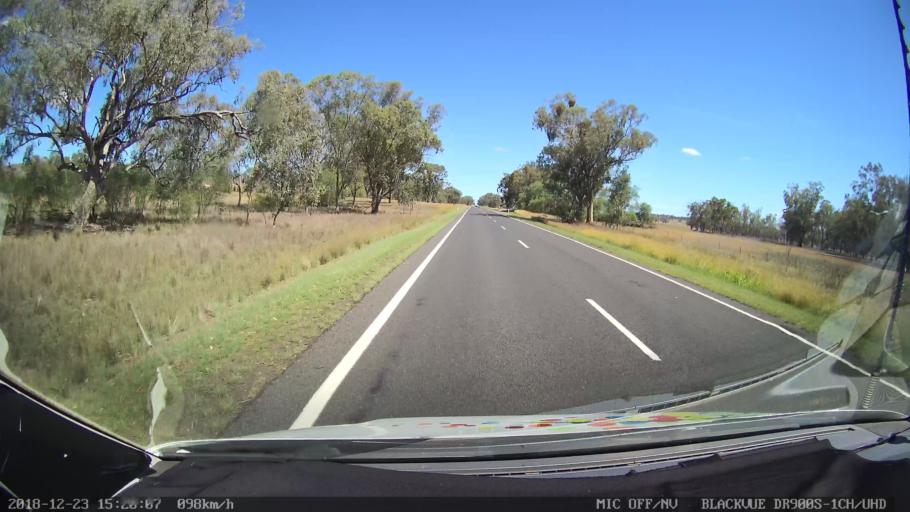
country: AU
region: New South Wales
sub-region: Tamworth Municipality
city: Manilla
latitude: -30.8383
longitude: 150.7875
